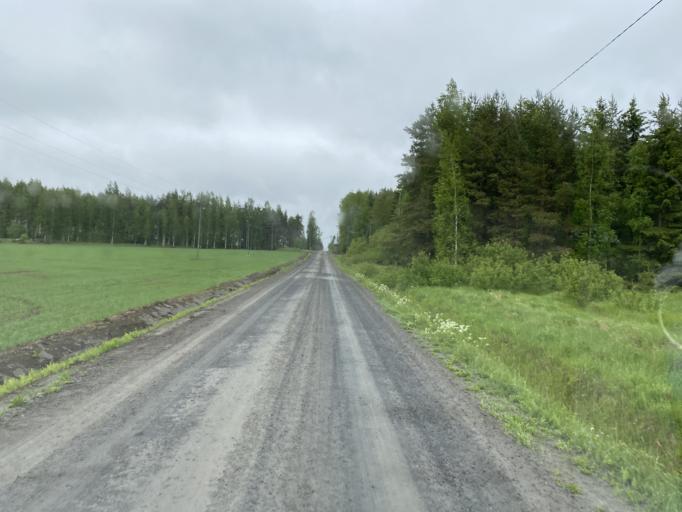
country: FI
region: Haeme
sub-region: Forssa
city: Forssa
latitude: 60.9383
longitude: 23.5857
